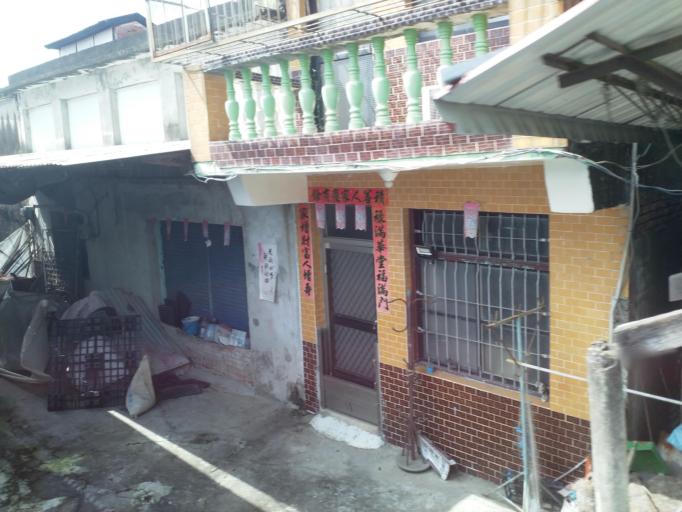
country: TW
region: Taiwan
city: Yujing
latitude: 22.9039
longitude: 120.5214
